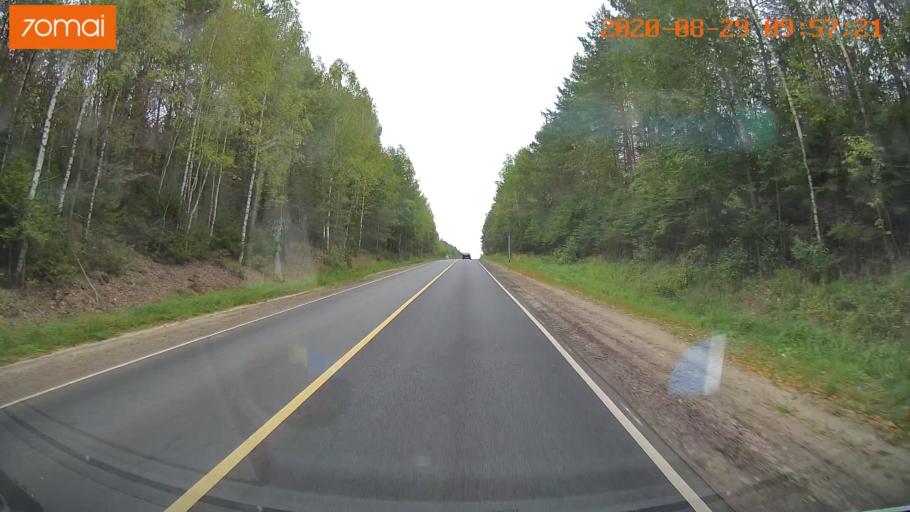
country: RU
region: Ivanovo
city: Zarechnyy
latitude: 57.4167
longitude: 42.3114
